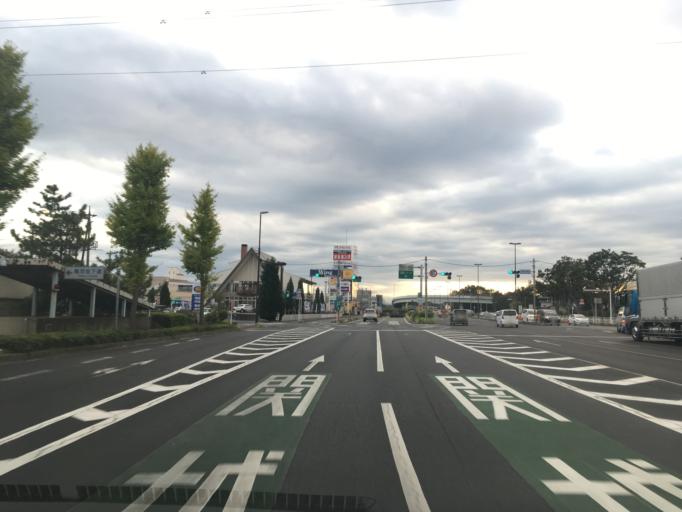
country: JP
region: Gunma
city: Maebashi-shi
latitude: 36.3771
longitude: 139.0350
